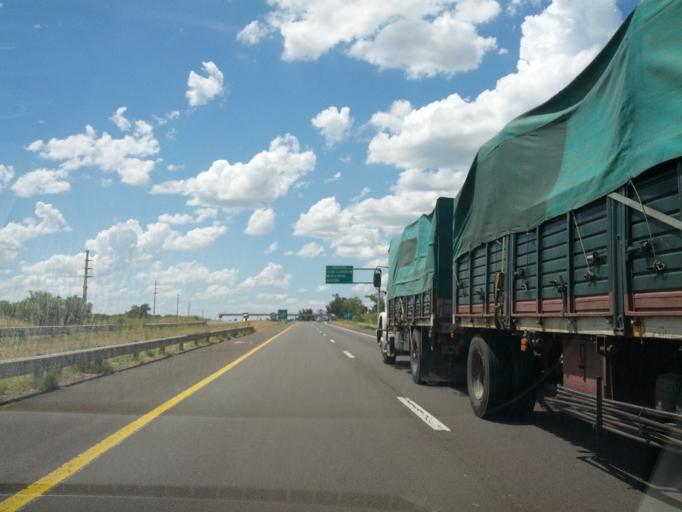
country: AR
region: Entre Rios
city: Concepcion del Uruguay
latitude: -32.4105
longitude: -58.2795
